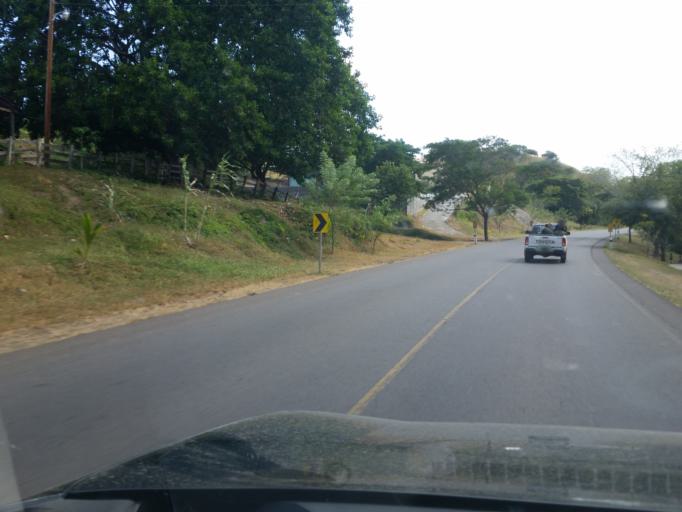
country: NI
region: Chontales
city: Comalapa
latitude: 12.1885
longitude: -85.5987
